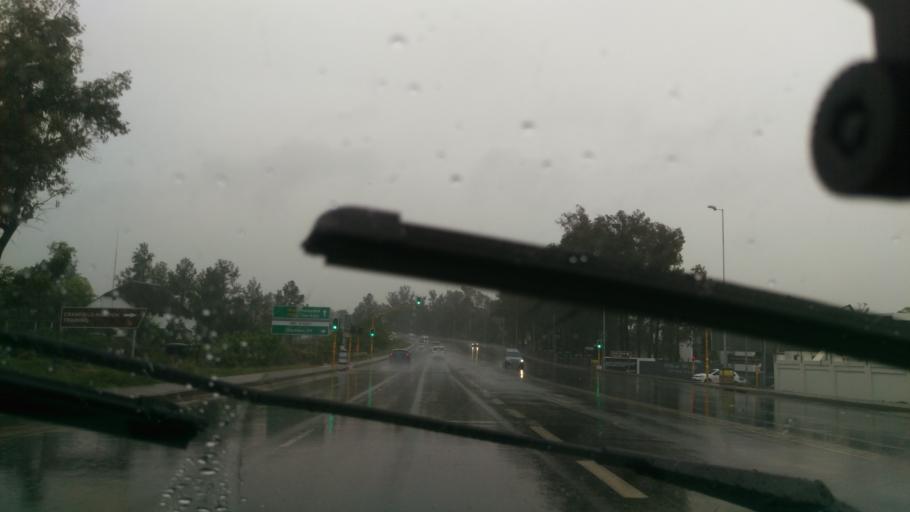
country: ZA
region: Gauteng
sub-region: City of Johannesburg Metropolitan Municipality
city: Diepsloot
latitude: -25.9943
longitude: 27.9831
